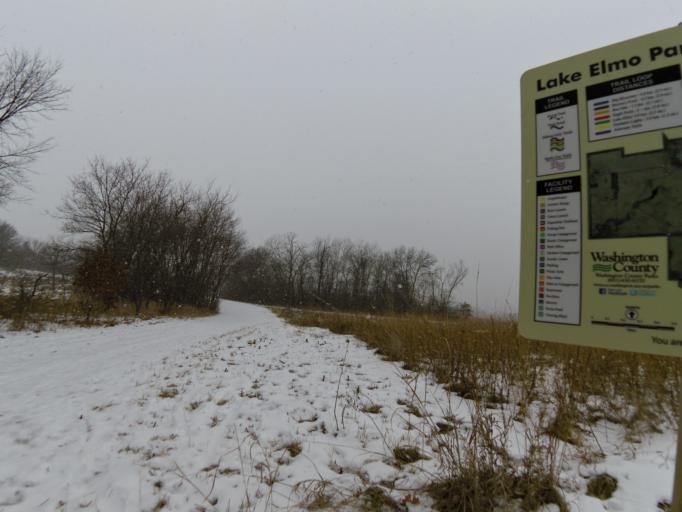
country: US
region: Minnesota
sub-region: Washington County
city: Lake Elmo
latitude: 44.9809
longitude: -92.9089
